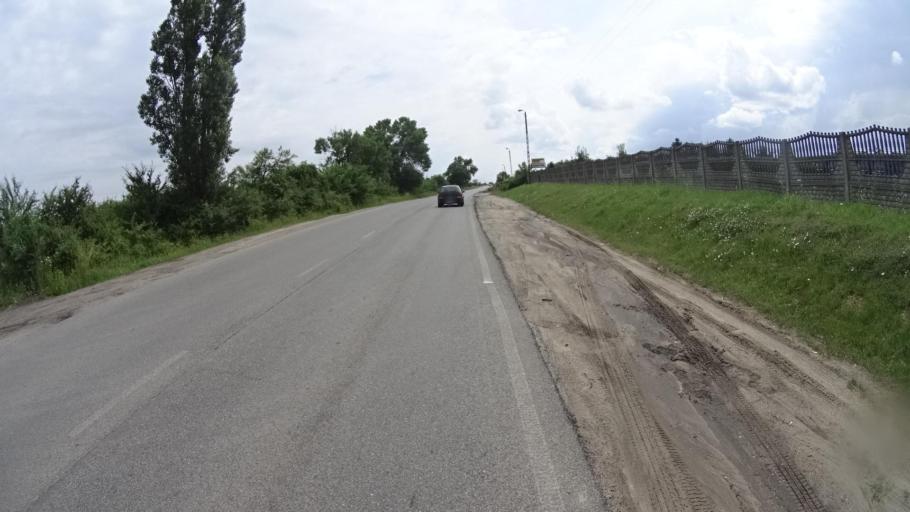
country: PL
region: Masovian Voivodeship
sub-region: Powiat grojecki
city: Grojec
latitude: 51.8944
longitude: 20.8621
